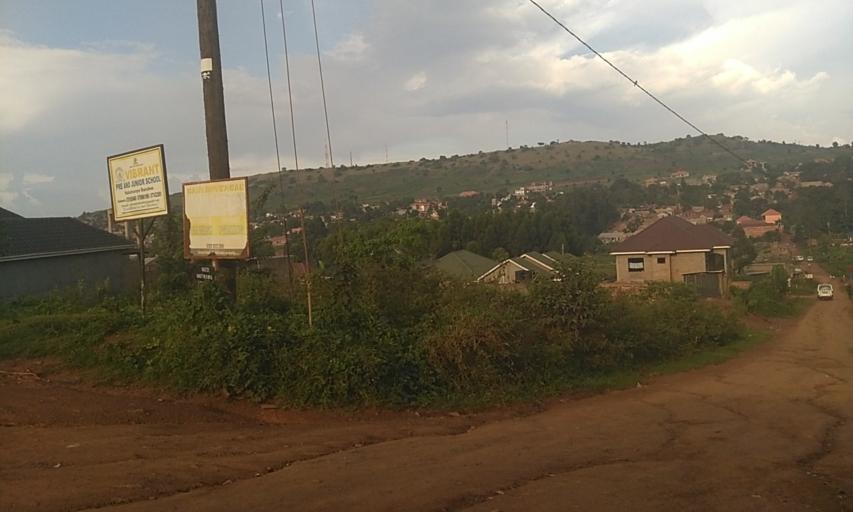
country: UG
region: Central Region
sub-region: Wakiso District
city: Kajansi
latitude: 0.2731
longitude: 32.5244
